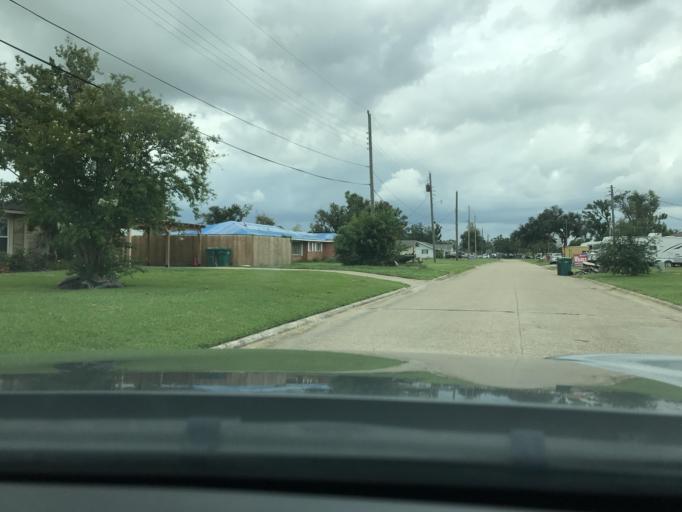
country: US
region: Louisiana
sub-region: Calcasieu Parish
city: Westlake
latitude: 30.2478
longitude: -93.2549
